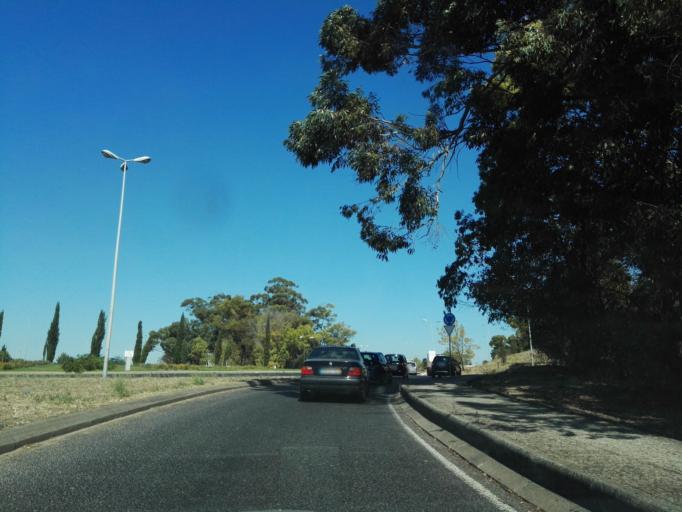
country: PT
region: Lisbon
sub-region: Odivelas
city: Pontinha
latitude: 38.7388
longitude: -9.2022
